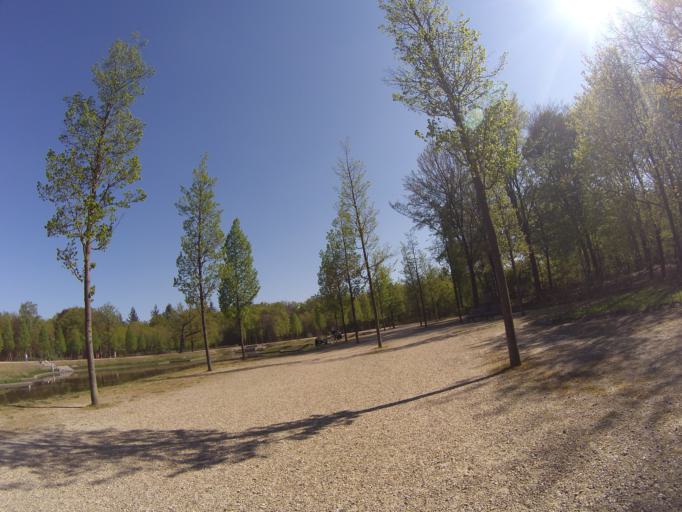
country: NL
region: Utrecht
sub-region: Gemeente Baarn
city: Baarn
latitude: 52.2045
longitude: 5.2820
